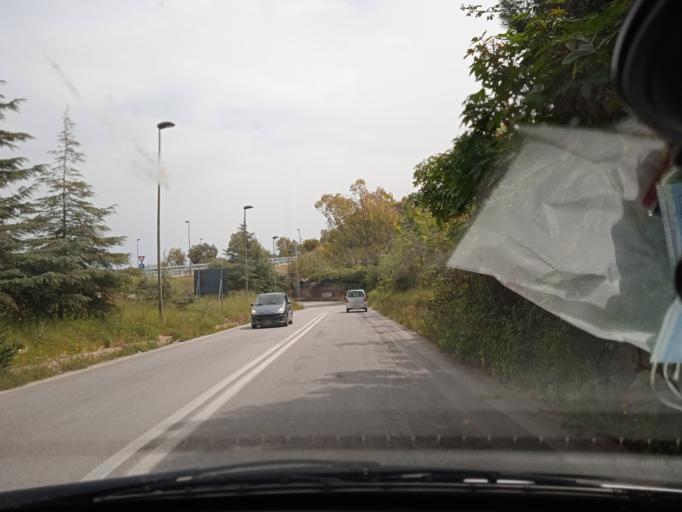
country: IT
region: Sicily
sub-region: Palermo
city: Altavilla Milicia
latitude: 38.0430
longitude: 13.5553
